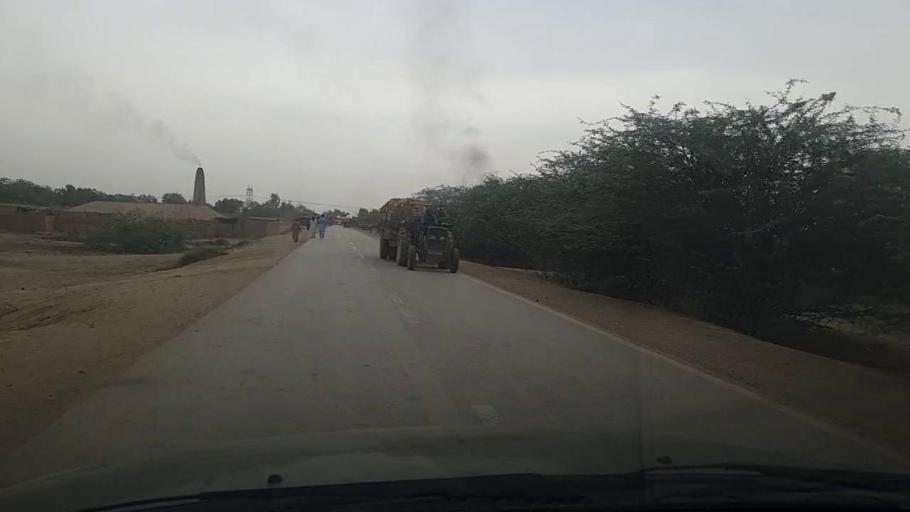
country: PK
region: Sindh
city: Daulatpur
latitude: 26.3403
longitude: 68.1230
